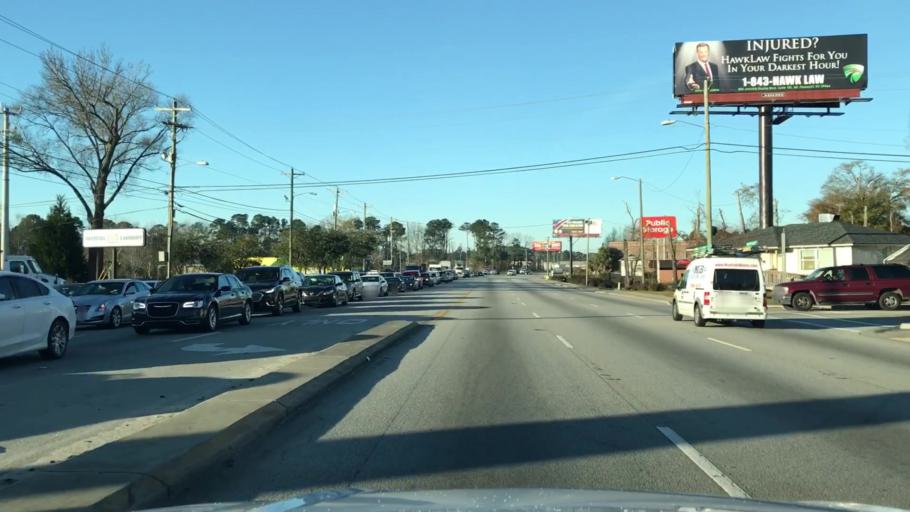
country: US
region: South Carolina
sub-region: Berkeley County
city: Hanahan
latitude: 32.9327
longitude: -80.0546
